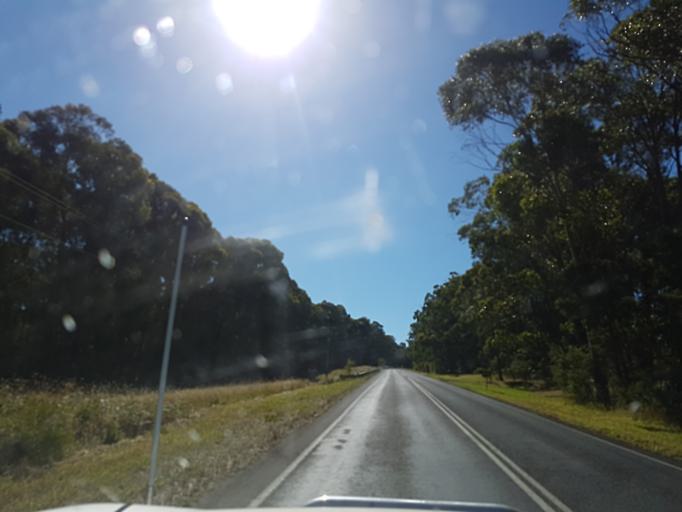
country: AU
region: Victoria
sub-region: Colac-Otway
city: Colac
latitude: -38.4566
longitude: 143.5854
